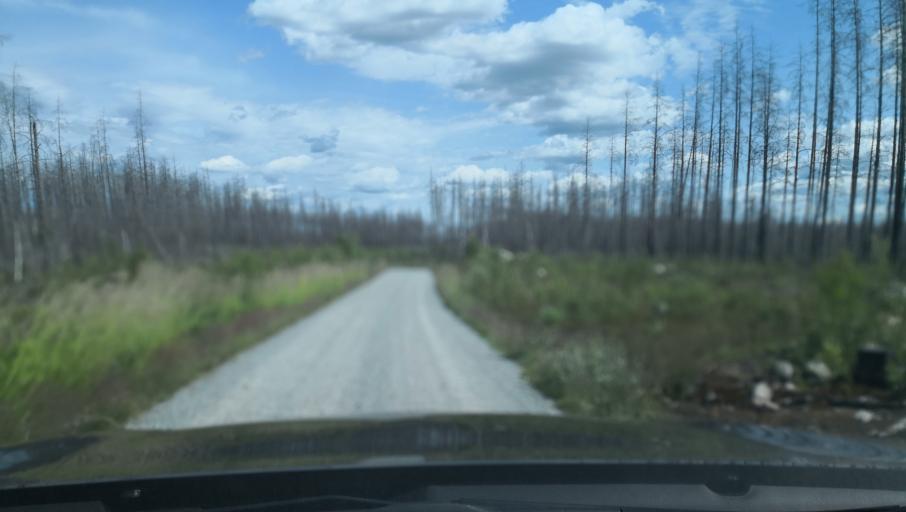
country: SE
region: Vaestmanland
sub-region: Surahammars Kommun
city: Ramnas
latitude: 59.8977
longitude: 16.1147
